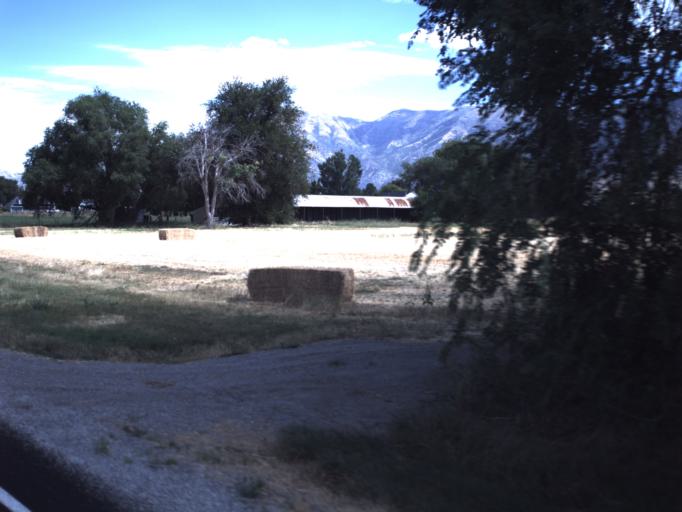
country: US
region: Utah
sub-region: Box Elder County
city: Honeyville
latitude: 41.6030
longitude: -112.1273
